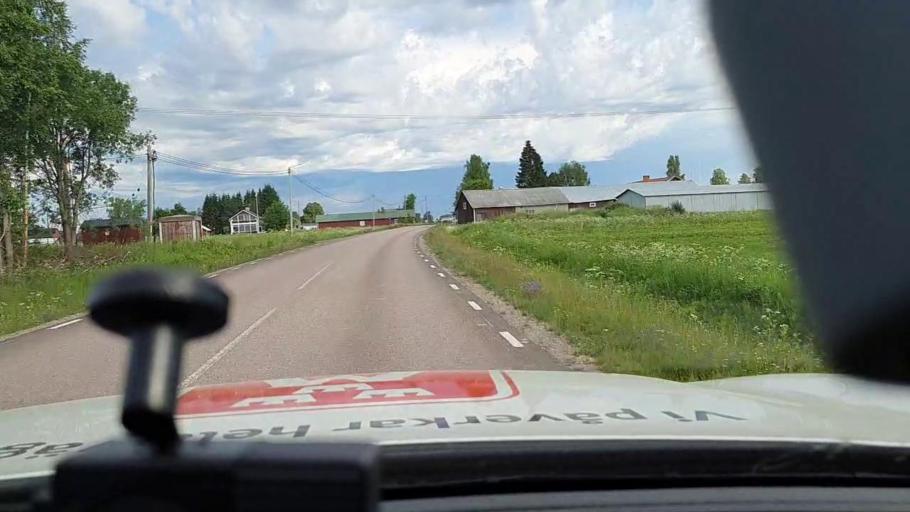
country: SE
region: Norrbotten
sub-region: Bodens Kommun
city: Saevast
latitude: 65.7019
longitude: 21.7699
